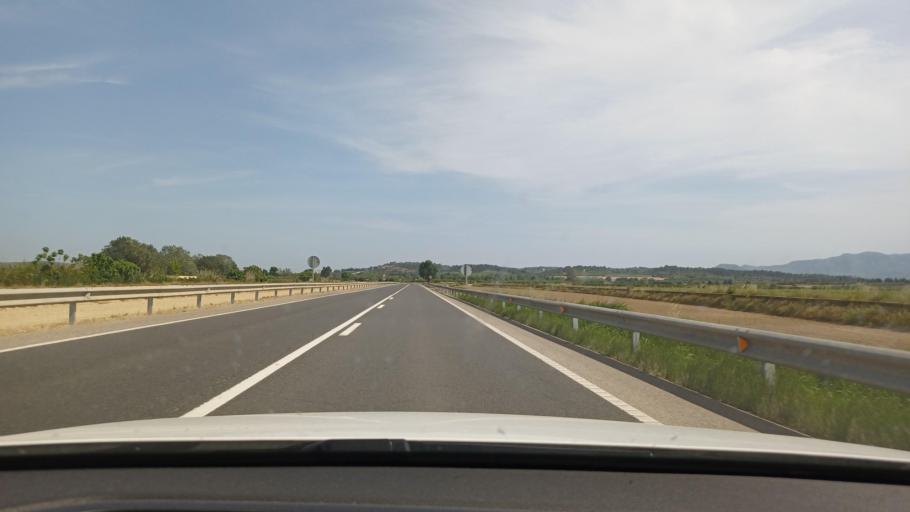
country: ES
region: Catalonia
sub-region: Provincia de Tarragona
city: Masdenverge
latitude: 40.7594
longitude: 0.5354
